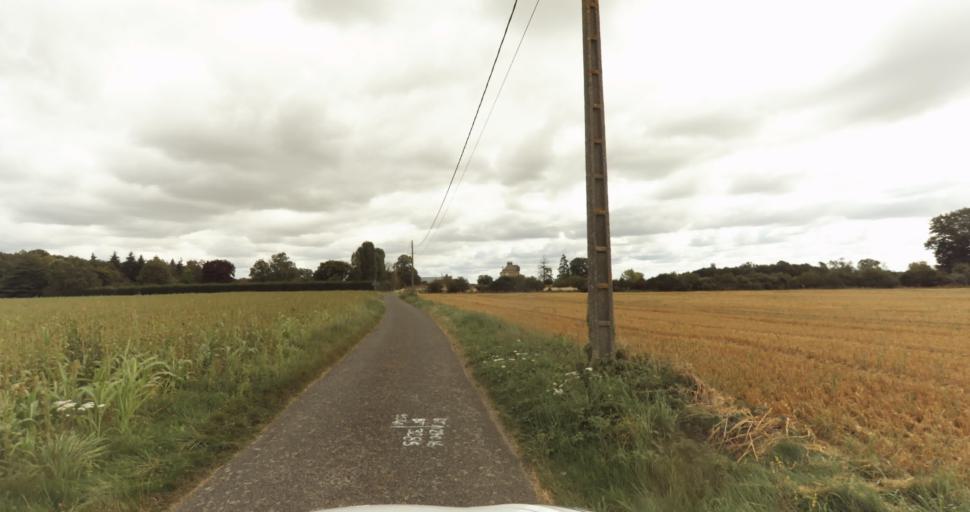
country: FR
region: Haute-Normandie
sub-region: Departement de l'Eure
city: Tillieres-sur-Avre
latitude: 48.7991
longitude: 1.1130
